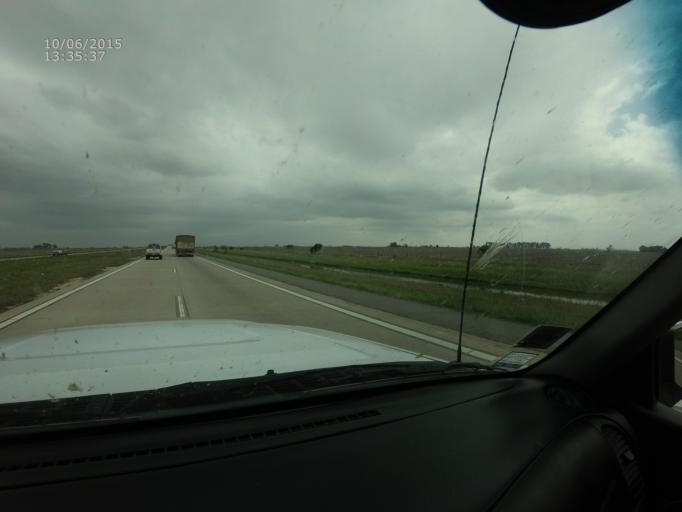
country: AR
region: Cordoba
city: Leones
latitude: -32.6155
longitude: -62.3752
